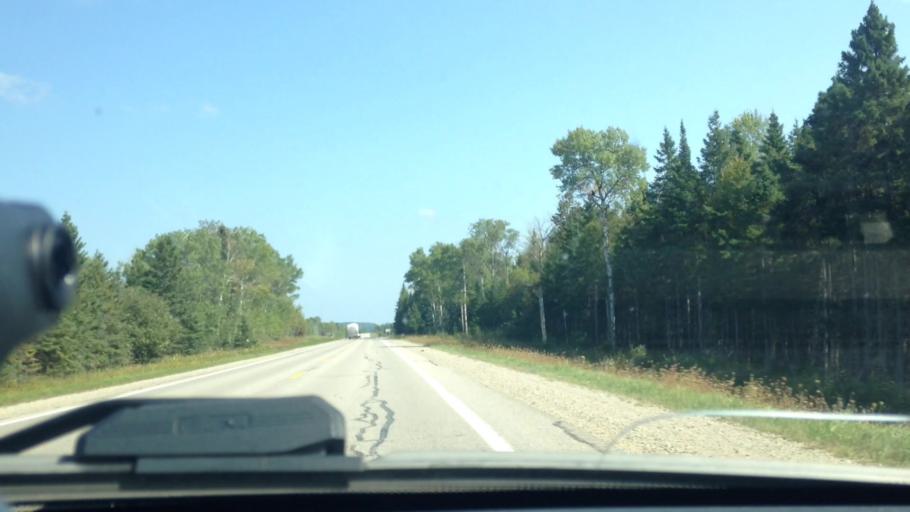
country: US
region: Michigan
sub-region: Luce County
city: Newberry
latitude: 46.3102
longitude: -85.6167
